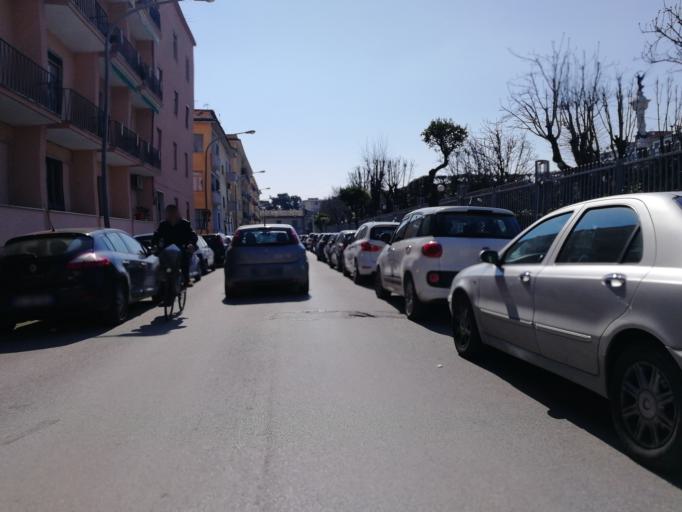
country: IT
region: Campania
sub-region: Provincia di Caserta
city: Santa Maria Capua Vetere
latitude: 41.0857
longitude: 14.2574
